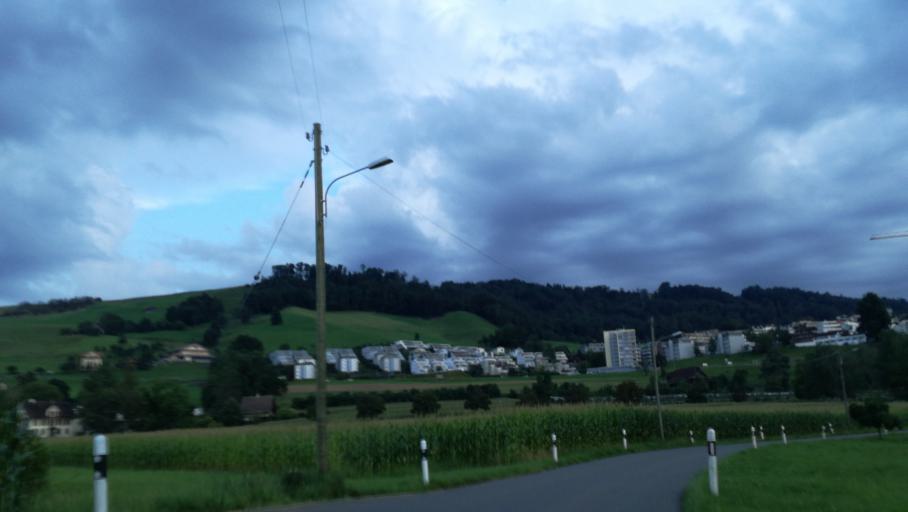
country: CH
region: Zug
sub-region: Zug
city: Zug
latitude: 47.1768
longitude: 8.5267
